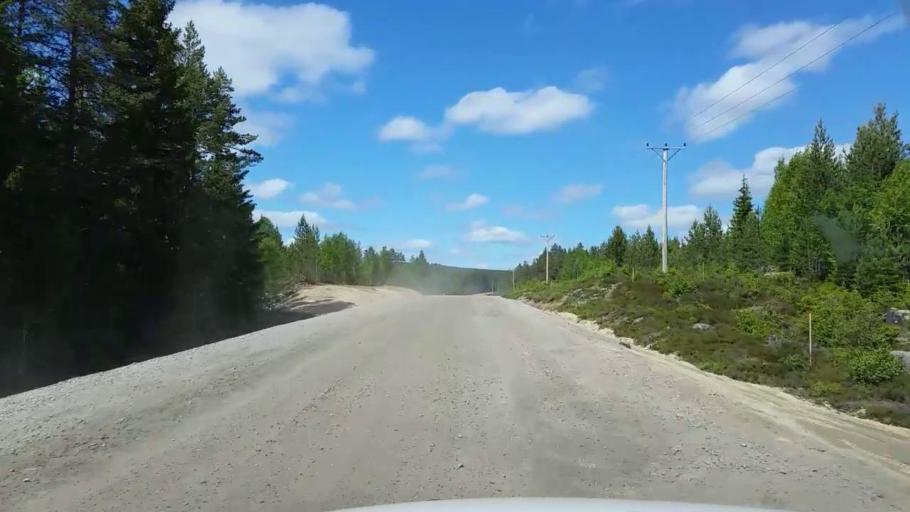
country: SE
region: Gaevleborg
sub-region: Ljusdals Kommun
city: Farila
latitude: 61.5931
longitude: 15.9213
